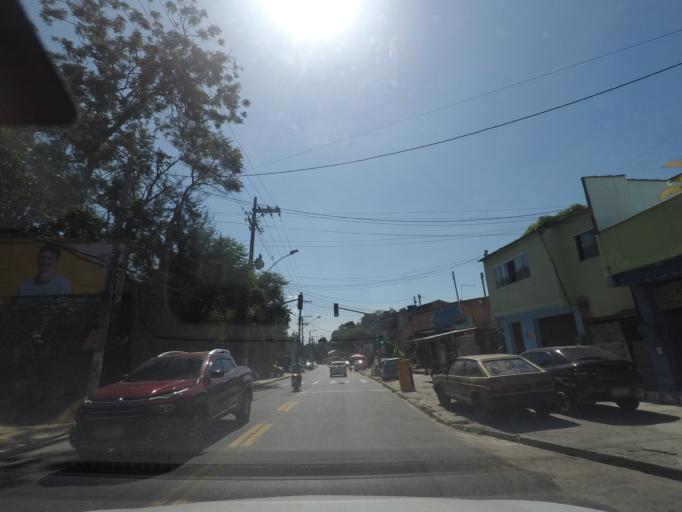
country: BR
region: Rio de Janeiro
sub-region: Niteroi
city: Niteroi
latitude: -22.9104
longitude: -43.0511
